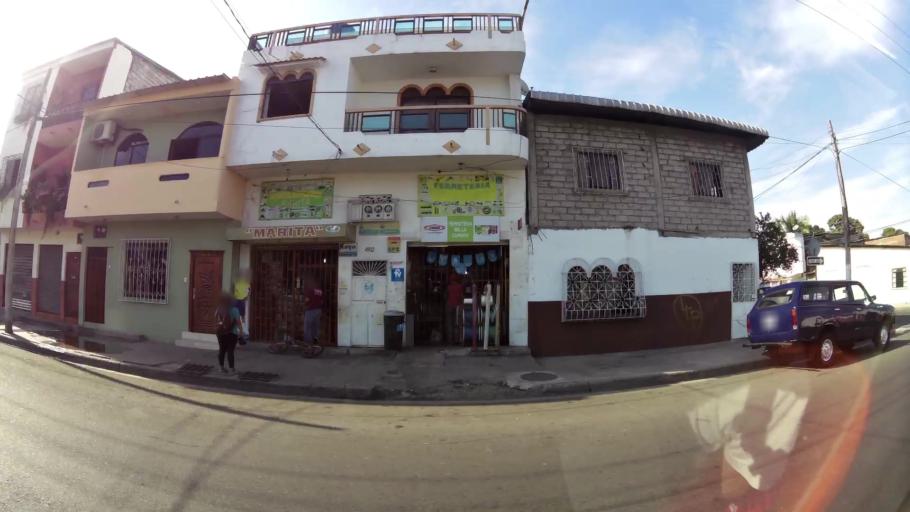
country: EC
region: Guayas
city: Guayaquil
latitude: -2.1934
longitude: -79.9169
